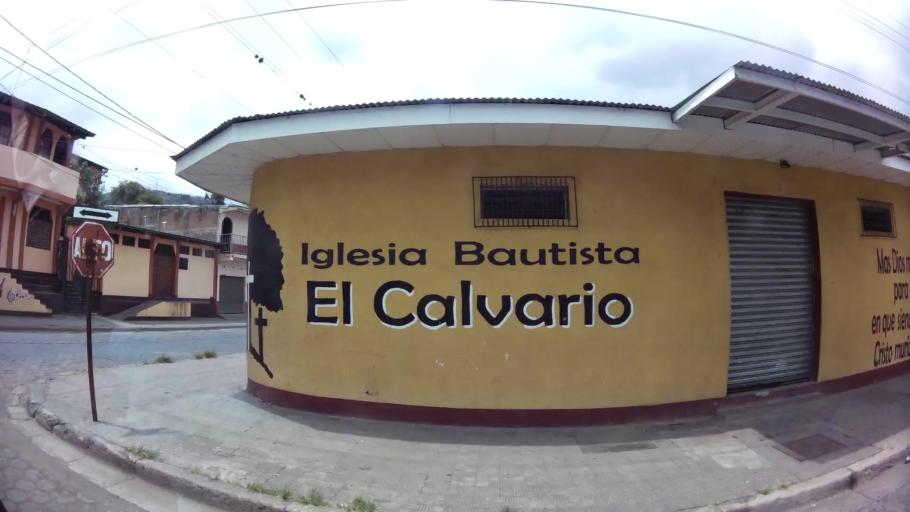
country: NI
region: Matagalpa
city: Matagalpa
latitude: 12.9297
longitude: -85.9127
